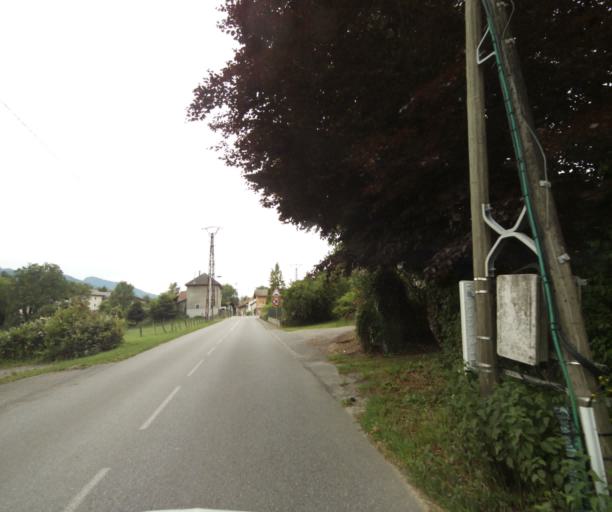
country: FR
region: Rhone-Alpes
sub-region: Departement de la Haute-Savoie
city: Allinges
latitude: 46.3302
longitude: 6.4745
